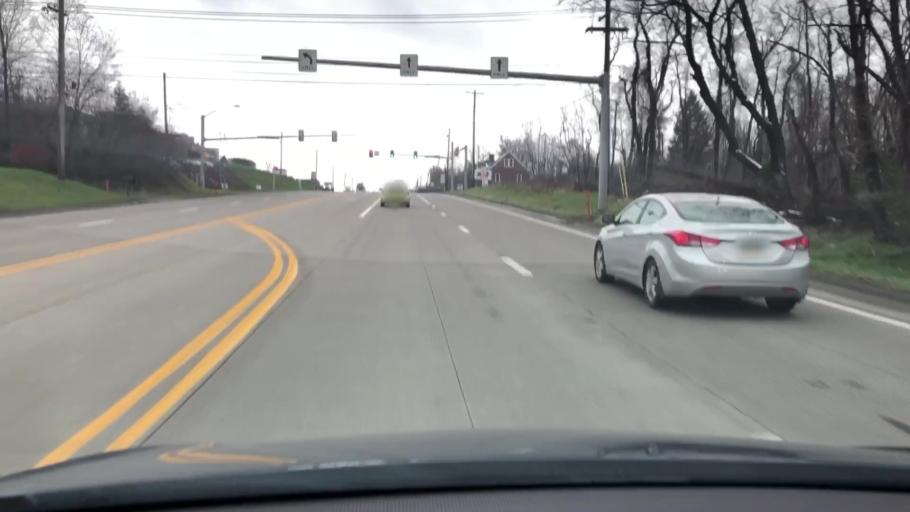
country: US
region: Pennsylvania
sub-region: Fayette County
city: Dunbar
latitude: 39.9510
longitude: -79.6536
